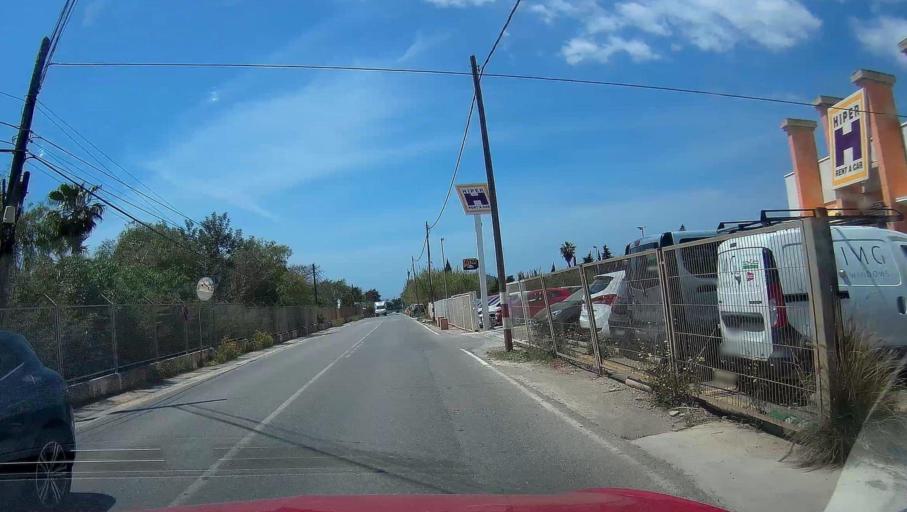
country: ES
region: Balearic Islands
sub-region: Illes Balears
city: Ibiza
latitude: 38.8785
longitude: 1.3680
